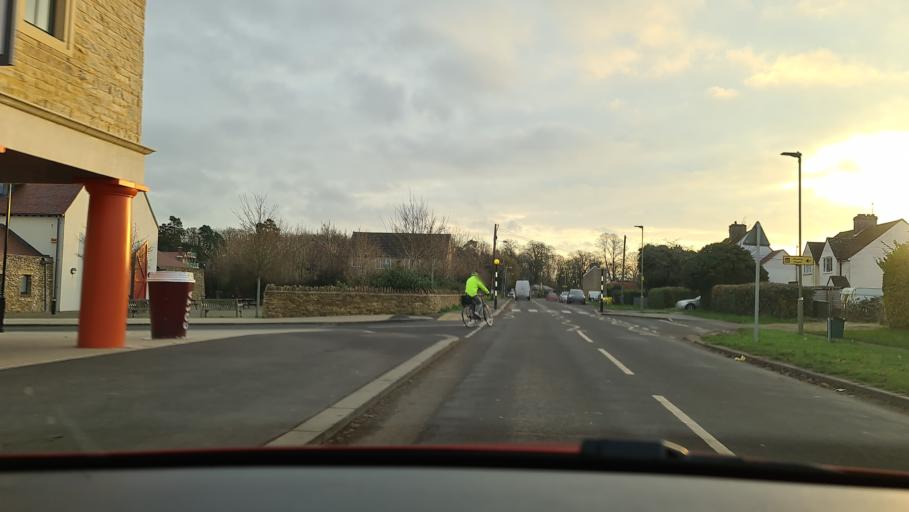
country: GB
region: England
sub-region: Oxfordshire
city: Kidlington
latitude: 51.8561
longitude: -1.2761
